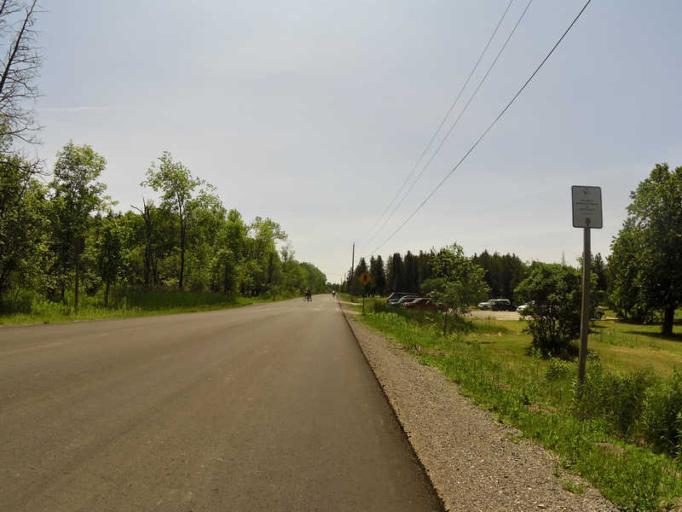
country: CA
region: Ontario
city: Peterborough
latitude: 44.3668
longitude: -78.2902
